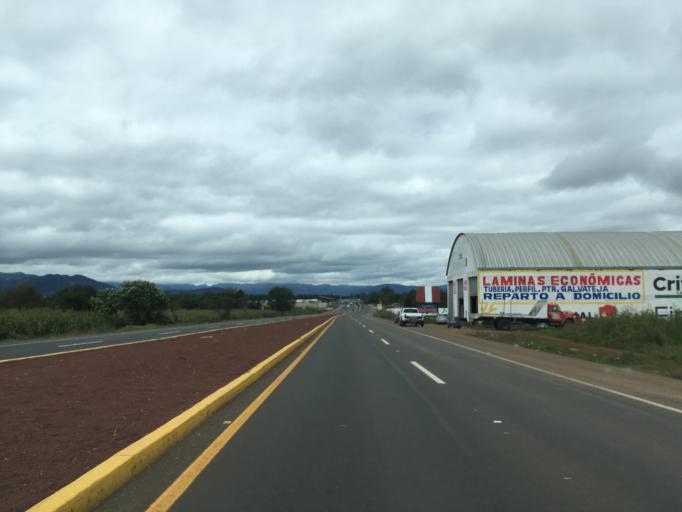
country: MX
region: Hidalgo
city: Atotonilco el Grande
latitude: 20.2957
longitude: -98.6671
